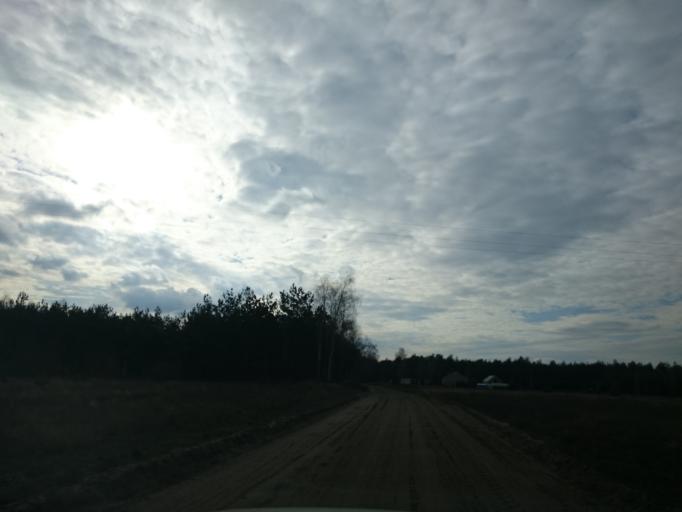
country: PL
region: Kujawsko-Pomorskie
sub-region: Powiat golubsko-dobrzynski
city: Ciechocin
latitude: 53.0493
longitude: 18.8721
